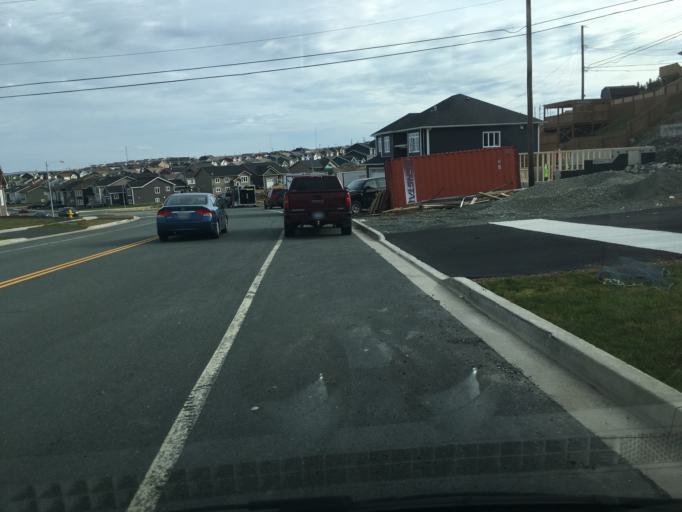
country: CA
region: Newfoundland and Labrador
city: Mount Pearl
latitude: 47.5554
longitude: -52.7989
